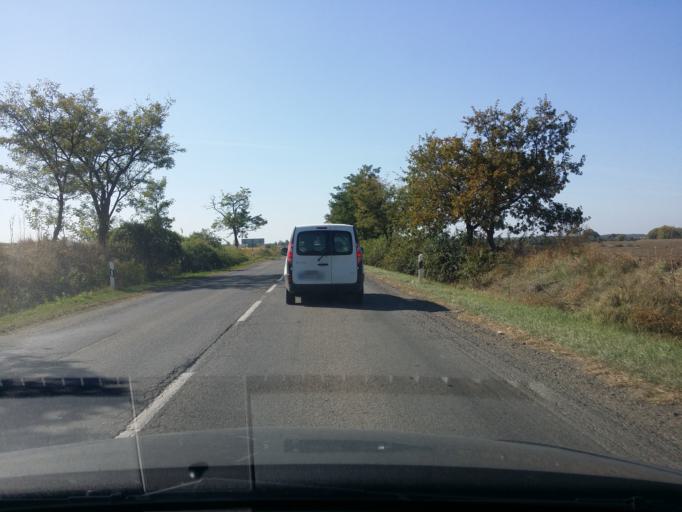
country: HU
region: Bacs-Kiskun
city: Tiszakecske
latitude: 46.8731
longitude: 20.1082
